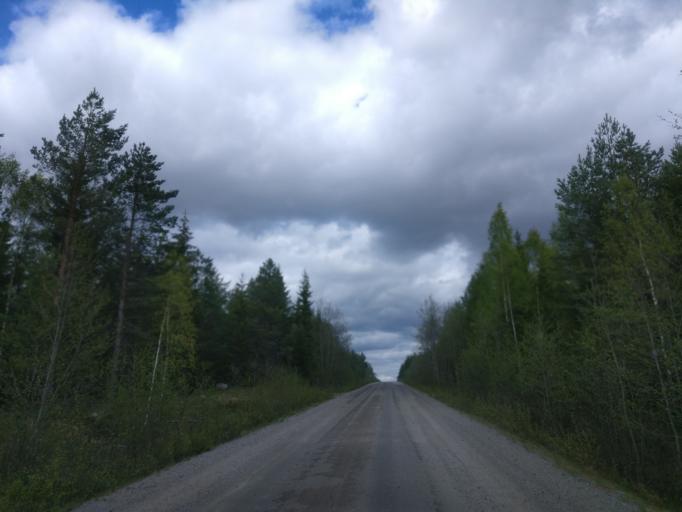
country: SE
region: Gaevleborg
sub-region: Soderhamns Kommun
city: Soderhamn
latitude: 61.4295
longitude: 16.9963
